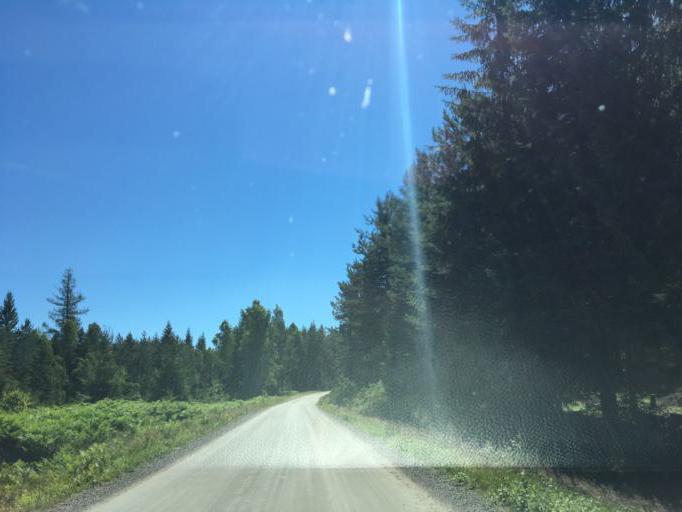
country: SE
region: Vaestra Goetaland
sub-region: Karlsborgs Kommun
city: Karlsborg
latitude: 58.7324
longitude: 14.5903
